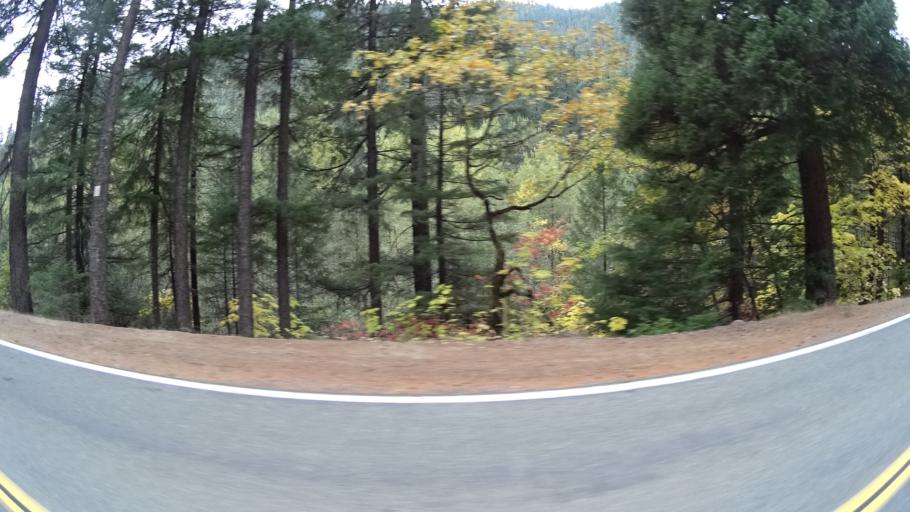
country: US
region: California
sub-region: Siskiyou County
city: Happy Camp
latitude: 41.8971
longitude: -123.4371
